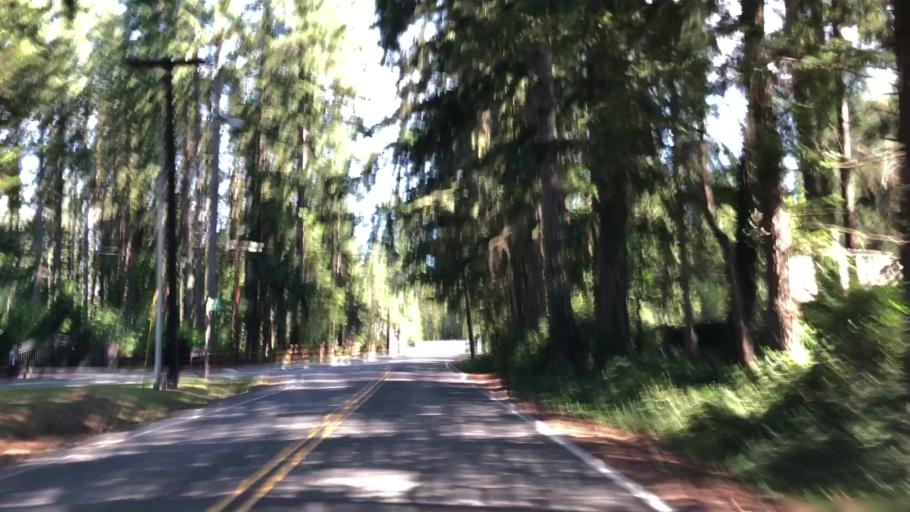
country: US
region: Washington
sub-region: King County
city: Cottage Lake
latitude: 47.7347
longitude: -122.0753
